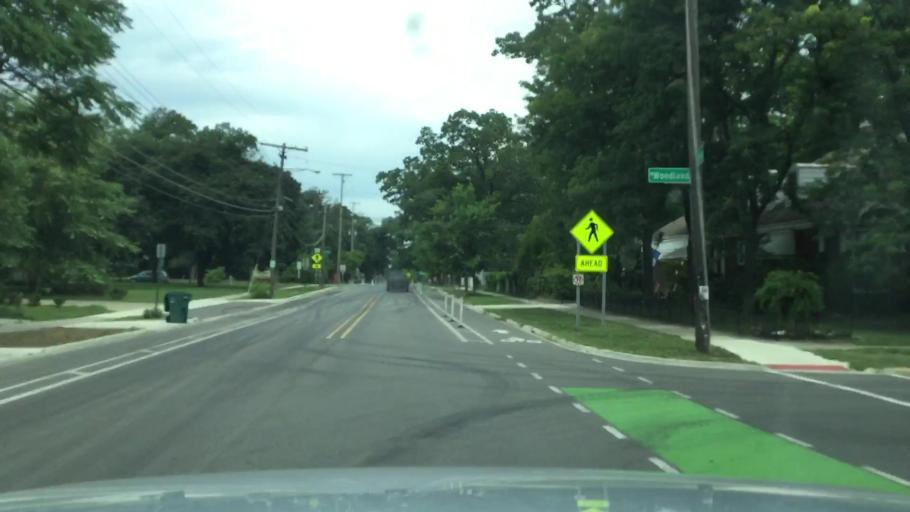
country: US
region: Michigan
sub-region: Oakland County
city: Pleasant Ridge
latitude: 42.4656
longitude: -83.1481
